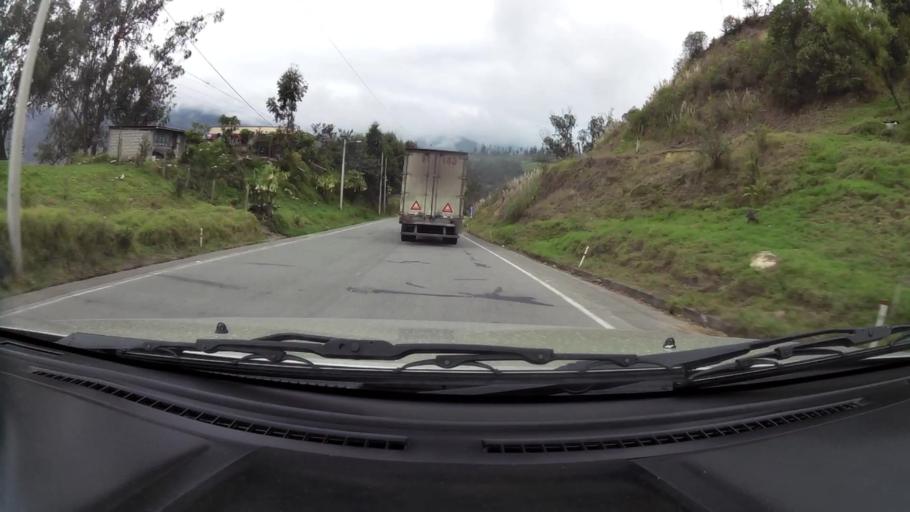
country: EC
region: Chimborazo
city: Alausi
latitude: -2.3051
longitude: -78.9262
